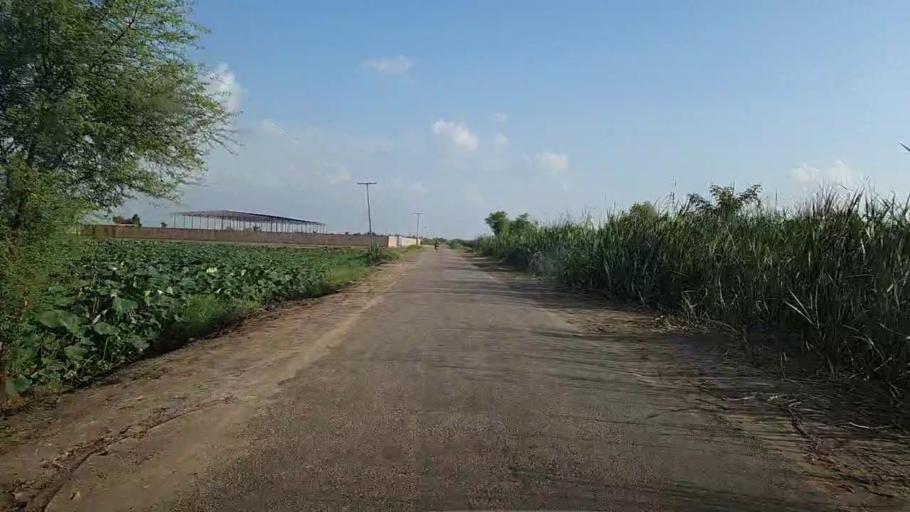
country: PK
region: Sindh
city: Hingorja
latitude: 27.0986
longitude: 68.4023
